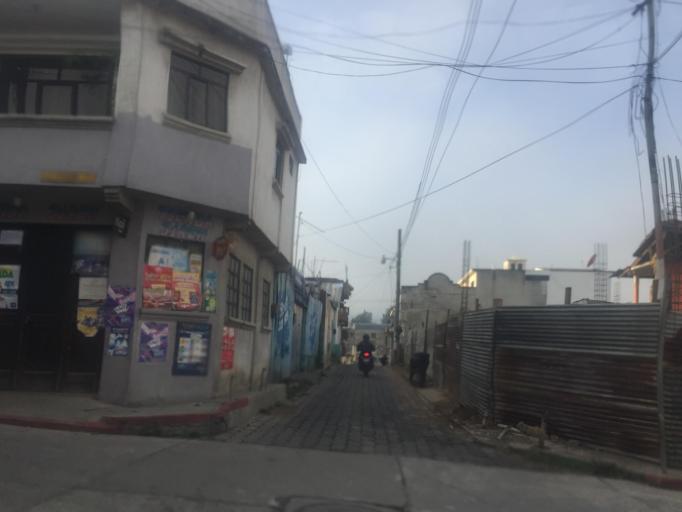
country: GT
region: Totonicapan
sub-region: Municipio de Totonicapan
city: Totonicapan
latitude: 14.9122
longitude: -91.3641
